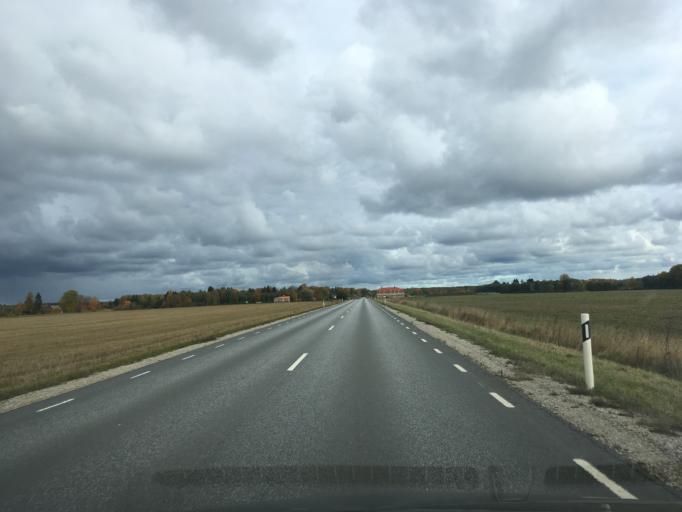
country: EE
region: Harju
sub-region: Anija vald
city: Kehra
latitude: 59.2749
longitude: 25.3613
